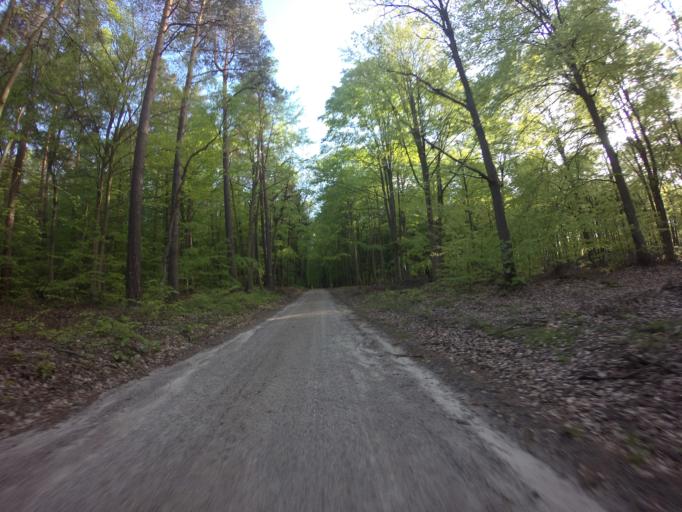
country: PL
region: West Pomeranian Voivodeship
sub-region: Powiat choszczenski
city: Drawno
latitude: 53.2022
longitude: 15.6720
